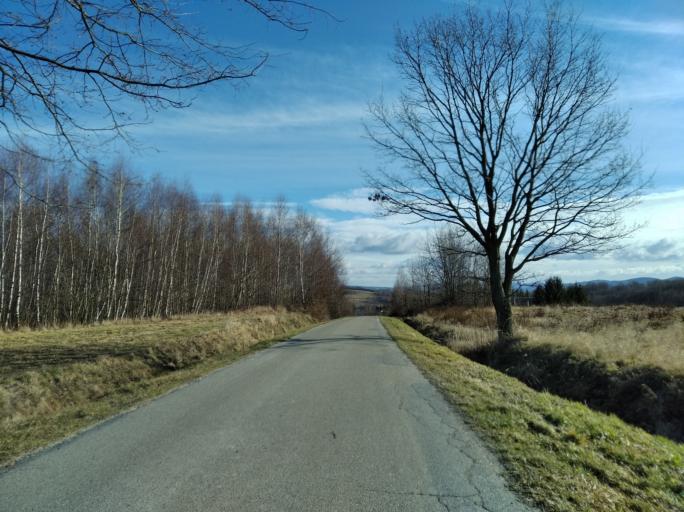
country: PL
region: Subcarpathian Voivodeship
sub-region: Powiat strzyzowski
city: Wisniowa
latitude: 49.9040
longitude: 21.6546
